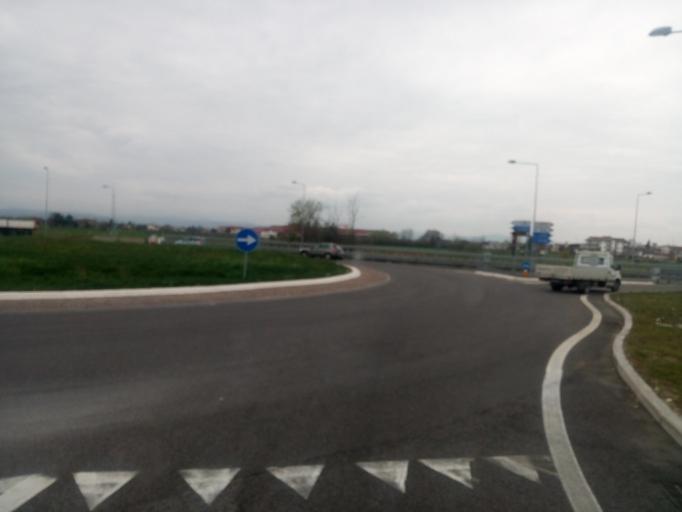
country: IT
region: Emilia-Romagna
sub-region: Forli-Cesena
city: Forli
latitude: 44.2493
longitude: 12.0903
